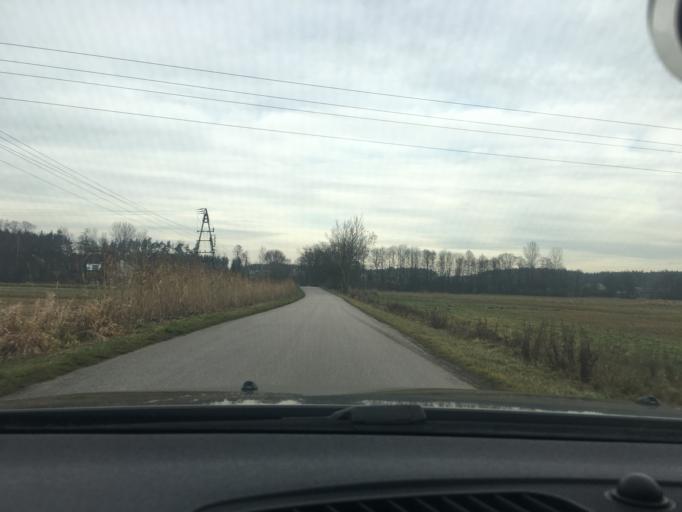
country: PL
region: Swietokrzyskie
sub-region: Powiat jedrzejowski
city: Imielno
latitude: 50.6379
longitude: 20.4148
